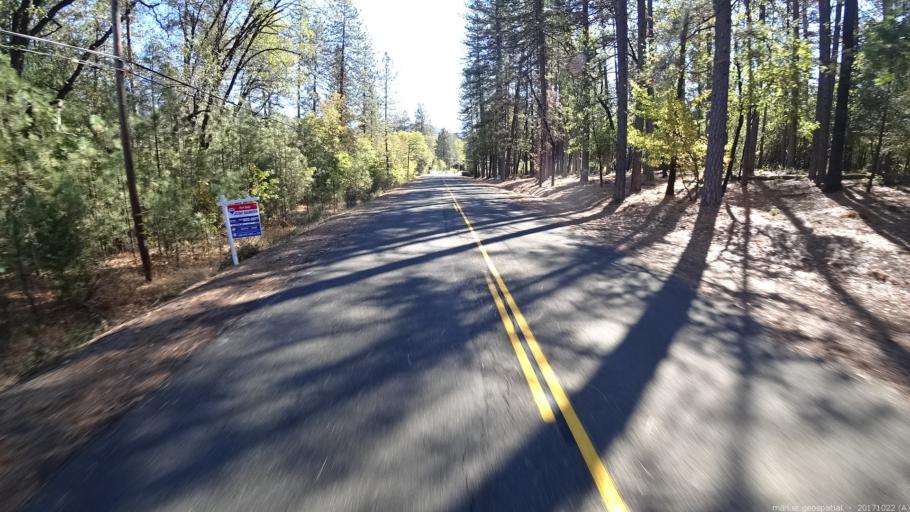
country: US
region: California
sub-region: Shasta County
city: Central Valley (historical)
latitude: 40.9145
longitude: -122.3846
